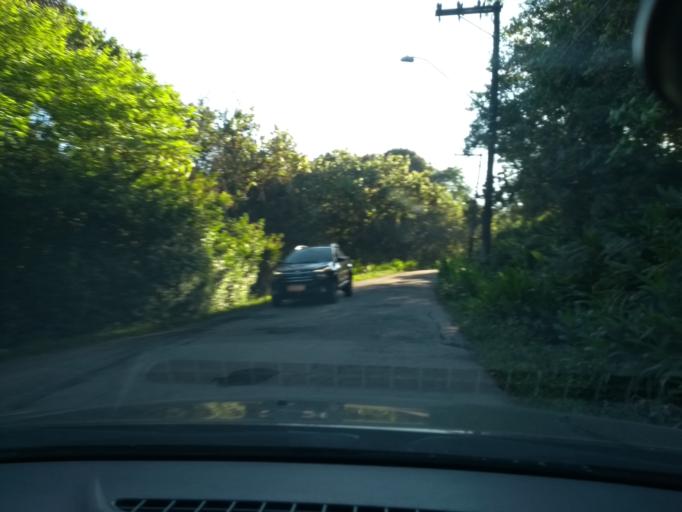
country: BR
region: Sao Paulo
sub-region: Sao Bernardo Do Campo
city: Sao Bernardo do Campo
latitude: -23.7780
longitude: -46.5121
